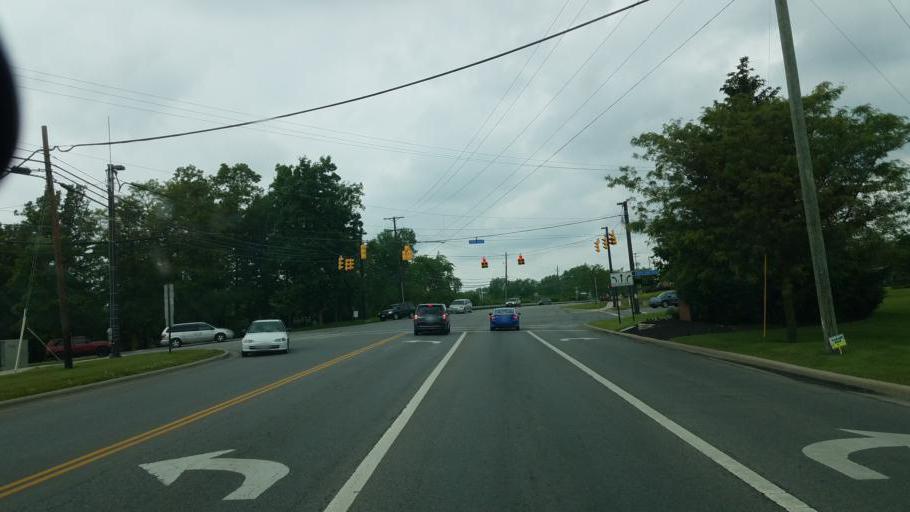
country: US
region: Ohio
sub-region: Delaware County
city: Delaware
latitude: 40.3092
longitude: -83.1087
